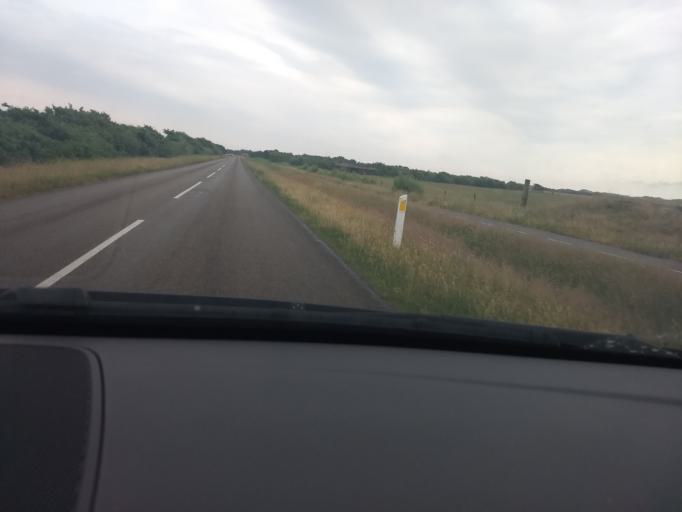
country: DK
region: South Denmark
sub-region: Fano Kommune
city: Nordby
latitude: 55.3659
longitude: 8.4564
